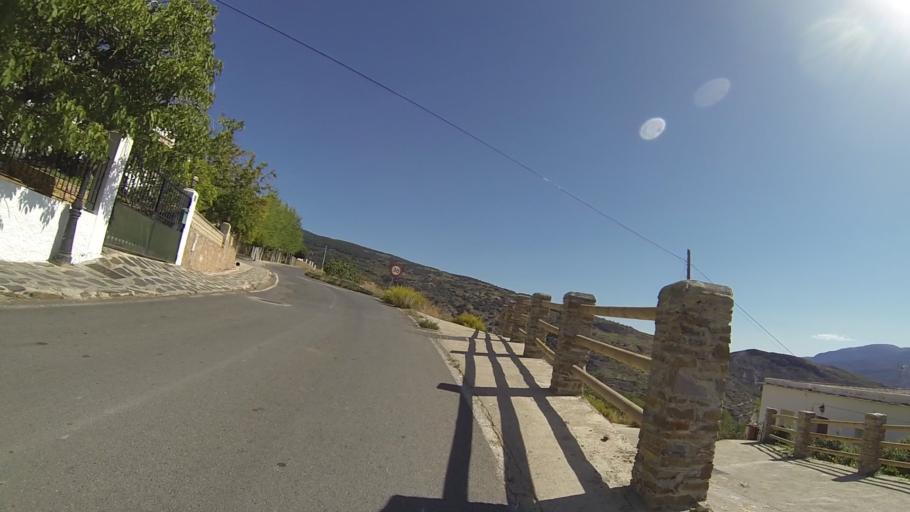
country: ES
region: Andalusia
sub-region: Provincia de Almeria
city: Bayarcal
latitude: 37.0077
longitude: -3.0104
